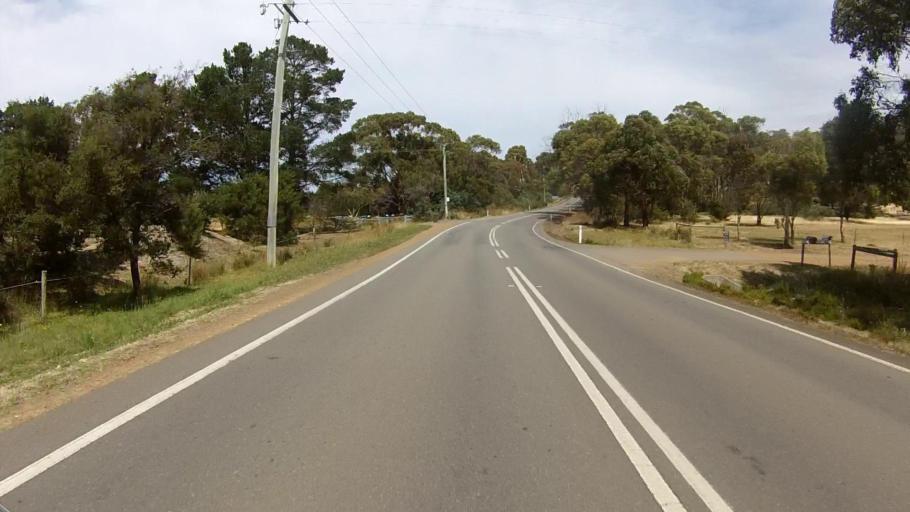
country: AU
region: Tasmania
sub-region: Clarence
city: Sandford
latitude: -43.0131
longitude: 147.4913
